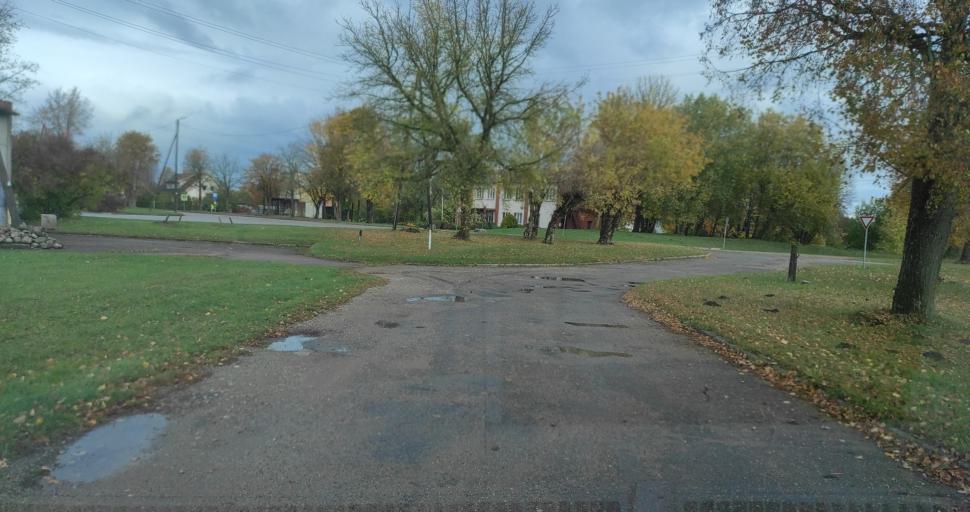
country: LV
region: Vainode
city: Vainode
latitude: 56.5685
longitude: 21.9008
